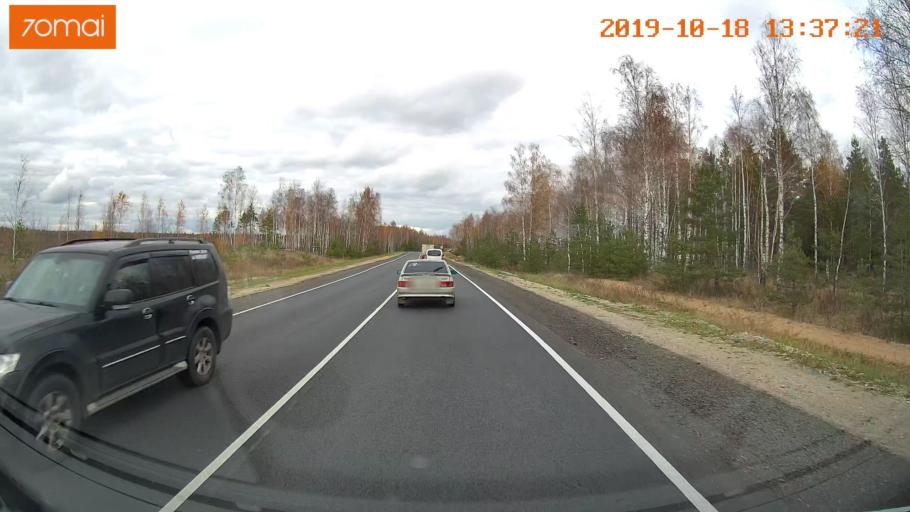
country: RU
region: Rjazan
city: Solotcha
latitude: 54.8784
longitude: 39.9947
